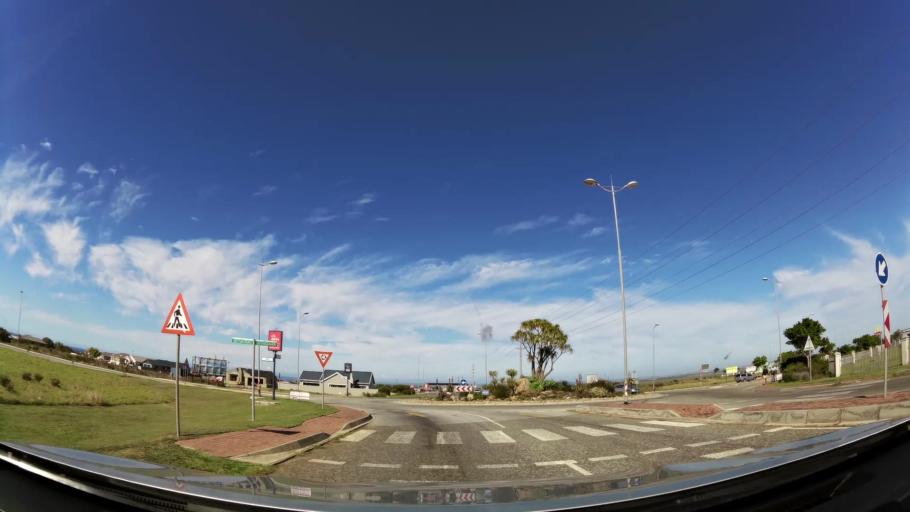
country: ZA
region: Eastern Cape
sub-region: Cacadu District Municipality
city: Jeffrey's Bay
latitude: -34.0316
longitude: 24.9009
